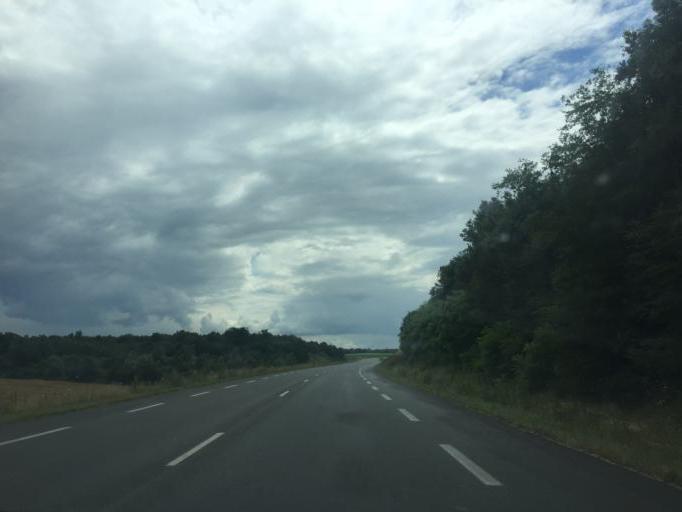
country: FR
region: Rhone-Alpes
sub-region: Departement de l'Isere
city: Janneyrias
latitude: 45.7830
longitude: 5.1323
